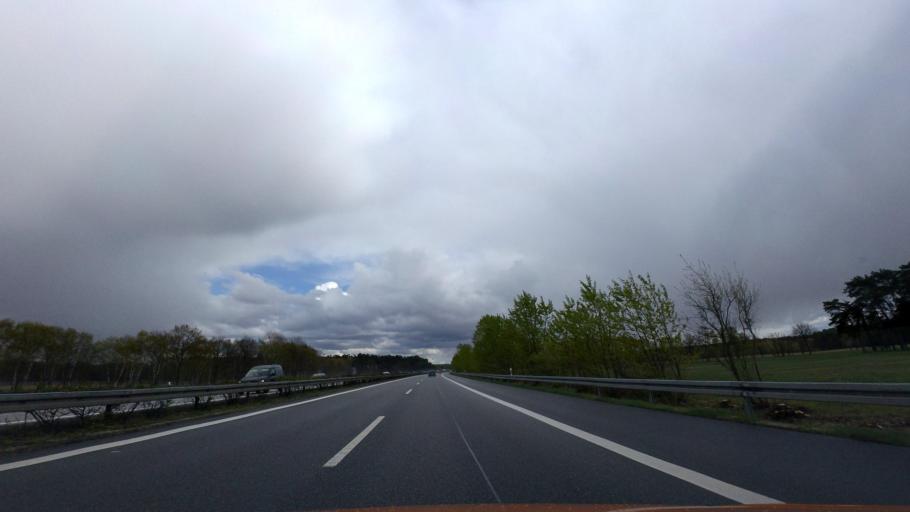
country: DE
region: Mecklenburg-Vorpommern
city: Sulstorf
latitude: 53.4675
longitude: 11.3308
